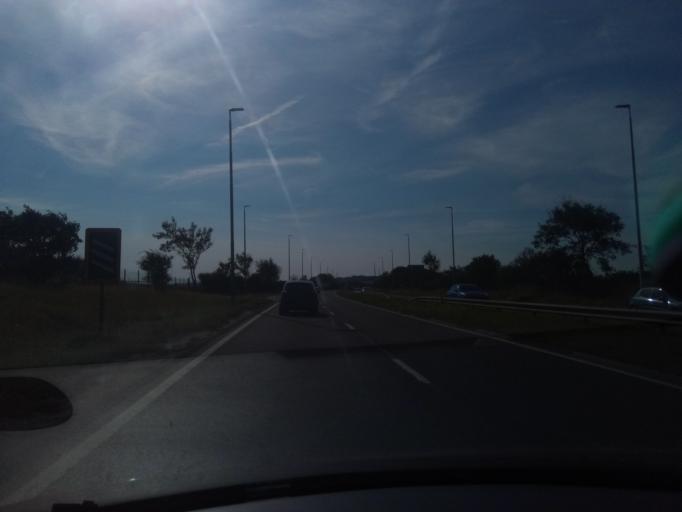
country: GB
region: England
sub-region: County Durham
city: Shotton
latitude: 54.7860
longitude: -1.3653
